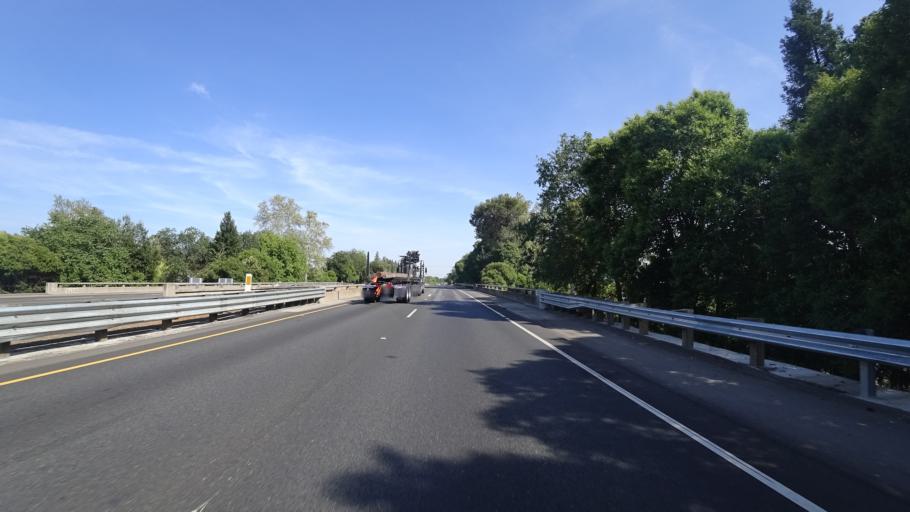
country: US
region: California
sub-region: Butte County
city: Chico
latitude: 39.7371
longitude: -121.8206
